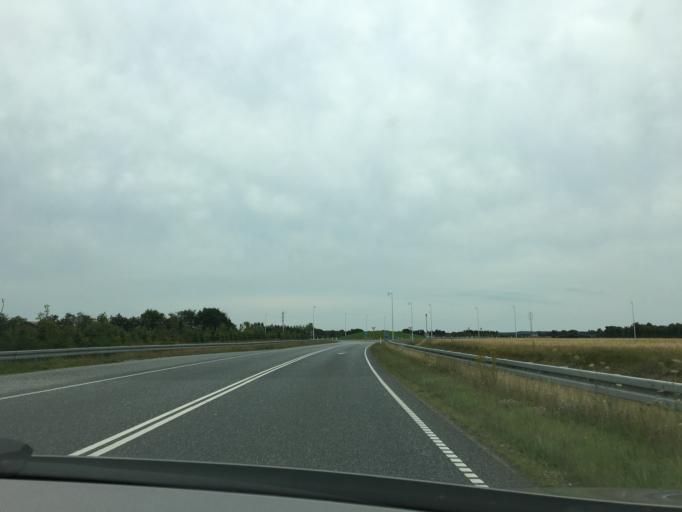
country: DK
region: Central Jutland
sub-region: Herning Kommune
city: Sunds
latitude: 56.2217
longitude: 9.0087
